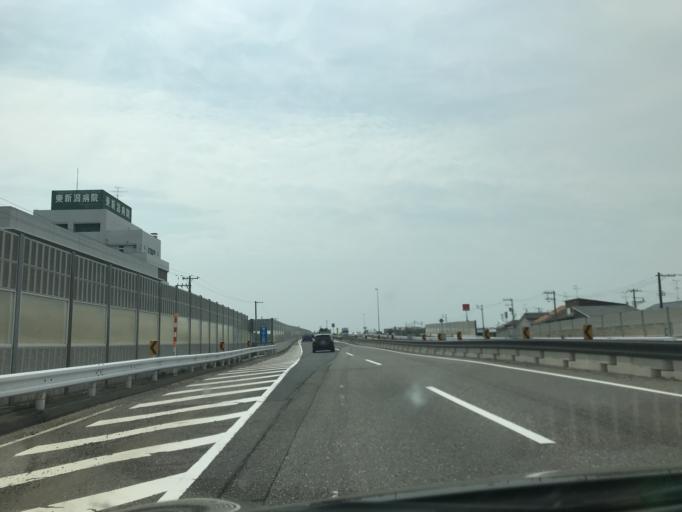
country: JP
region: Niigata
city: Kameda-honcho
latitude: 37.8853
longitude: 139.0786
